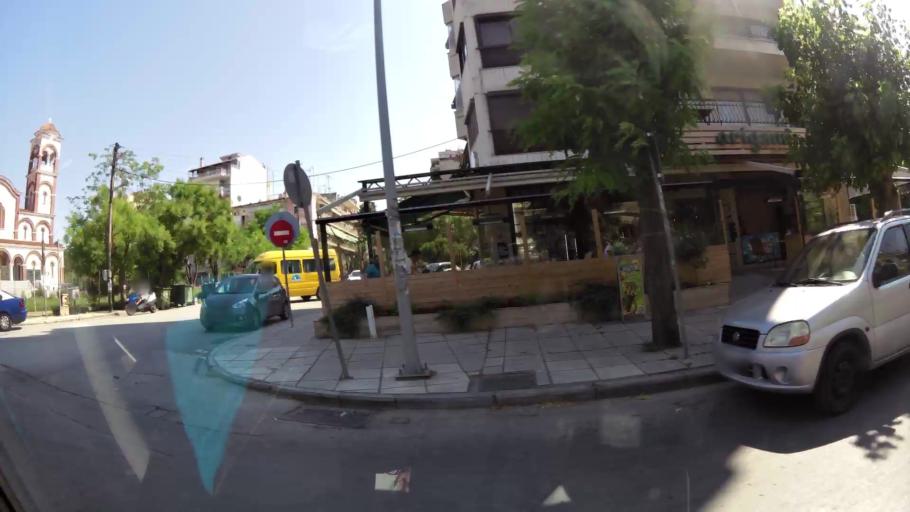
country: GR
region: Central Macedonia
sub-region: Nomos Thessalonikis
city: Kalamaria
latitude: 40.5828
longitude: 22.9629
